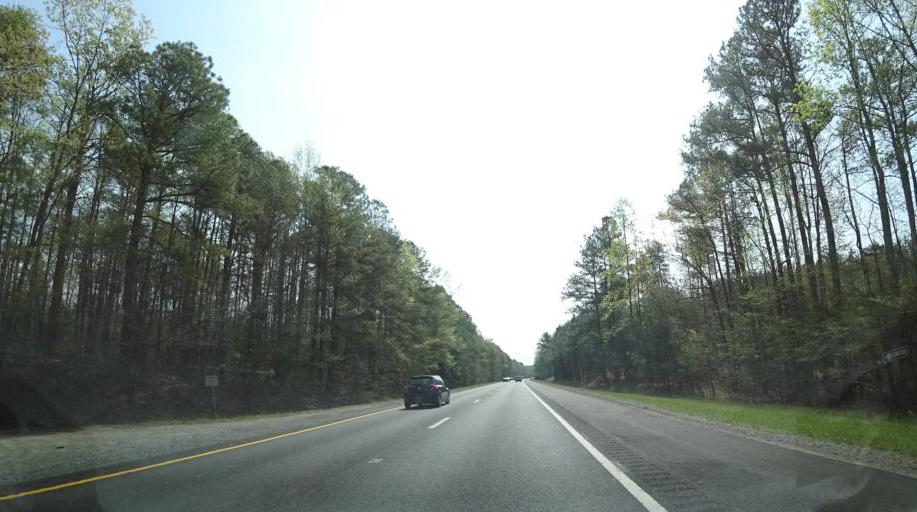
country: US
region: Virginia
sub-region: New Kent County
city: New Kent
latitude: 37.4754
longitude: -76.9123
